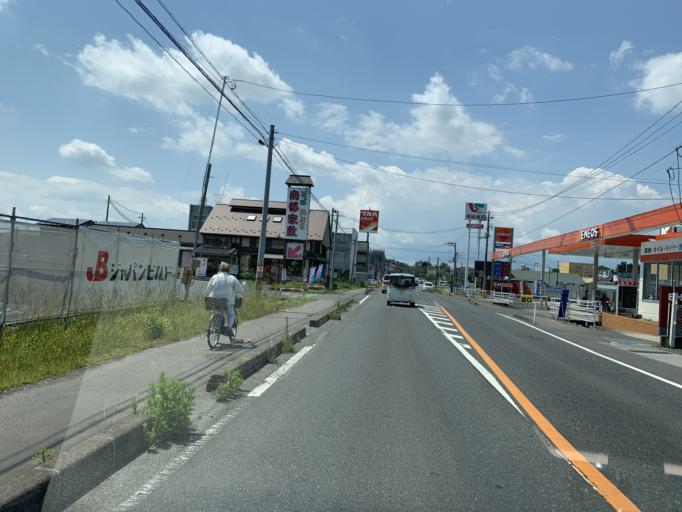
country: JP
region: Miyagi
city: Kogota
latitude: 38.5442
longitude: 141.0601
